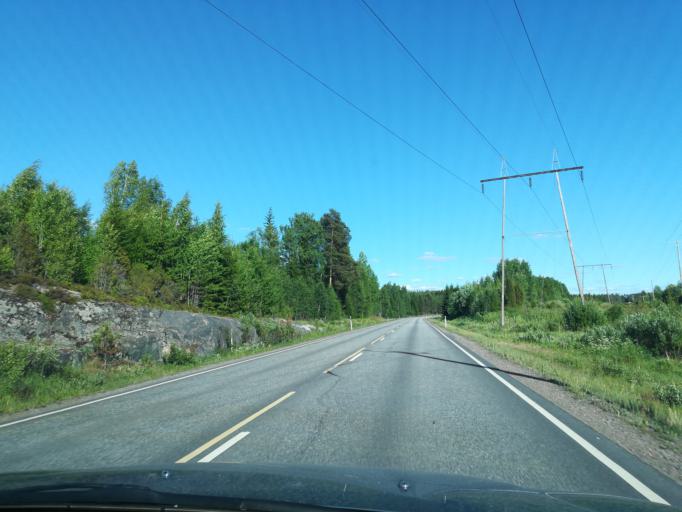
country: FI
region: South Karelia
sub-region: Imatra
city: Ruokolahti
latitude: 61.3501
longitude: 28.7527
